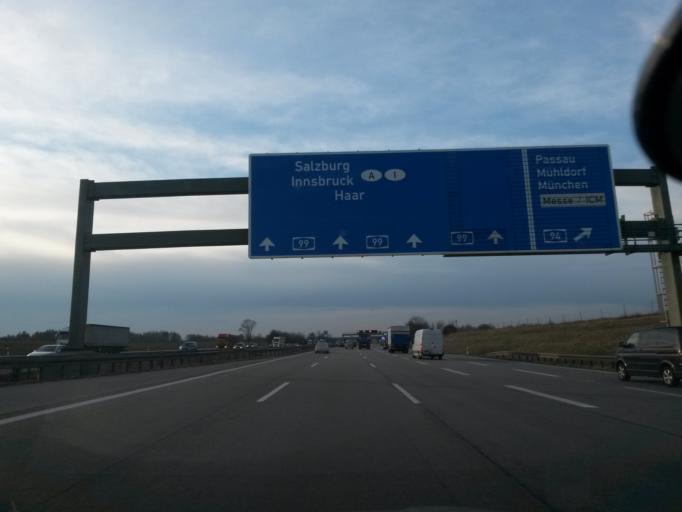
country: DE
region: Bavaria
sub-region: Upper Bavaria
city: Feldkirchen
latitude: 48.1489
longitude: 11.7552
